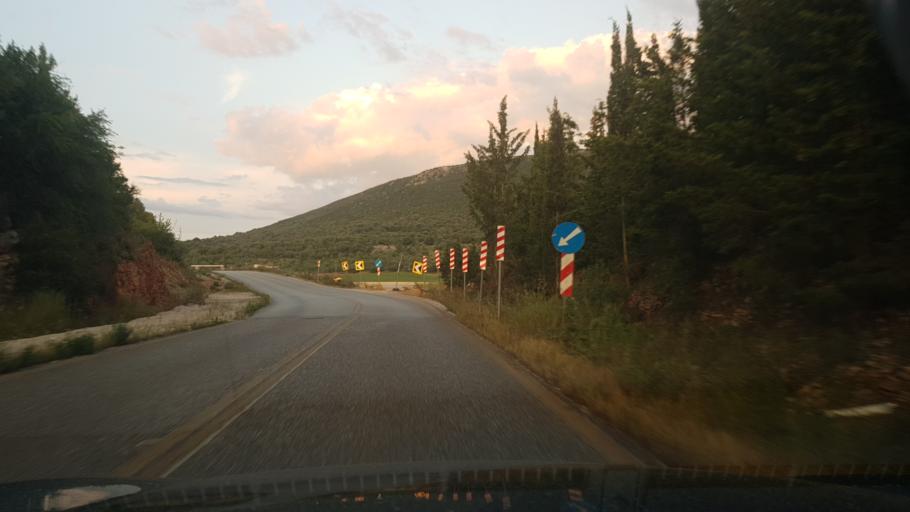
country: GR
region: West Greece
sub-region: Nomos Aitolias kai Akarnanias
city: Vonitsa
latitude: 38.8973
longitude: 20.8711
